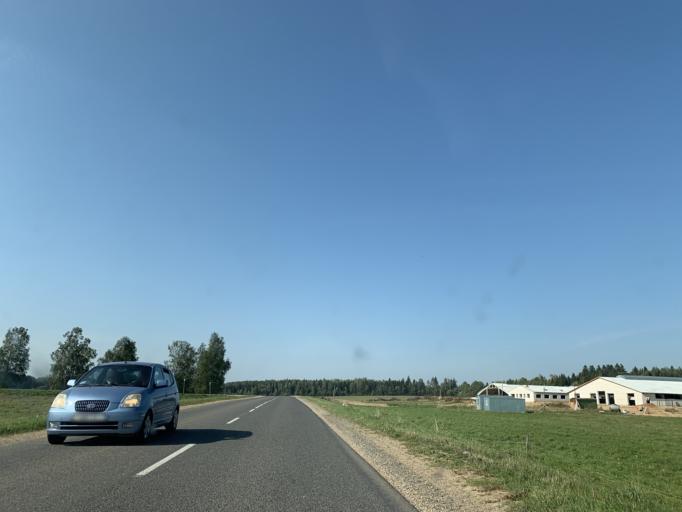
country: BY
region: Minsk
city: Rakaw
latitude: 53.8810
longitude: 26.9636
